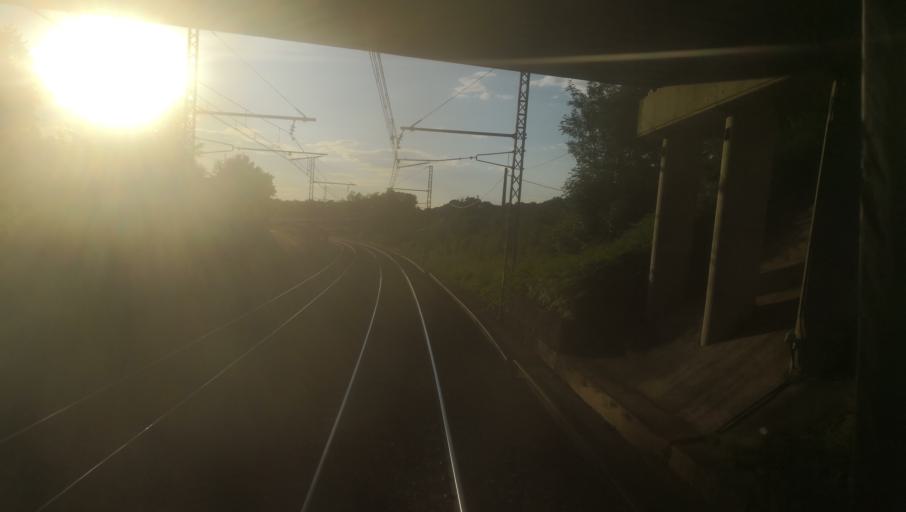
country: FR
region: Centre
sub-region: Departement de l'Indre
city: Chantome
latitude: 46.4927
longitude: 1.5345
